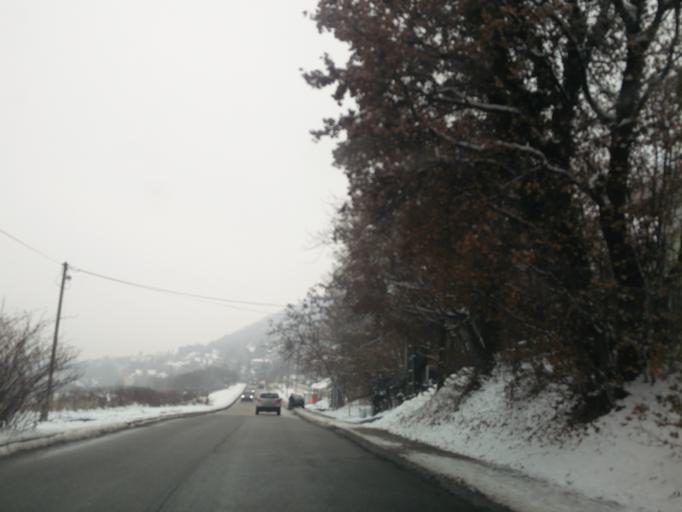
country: HU
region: Budapest
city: Budapest III. keruelet
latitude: 47.5430
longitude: 19.0204
